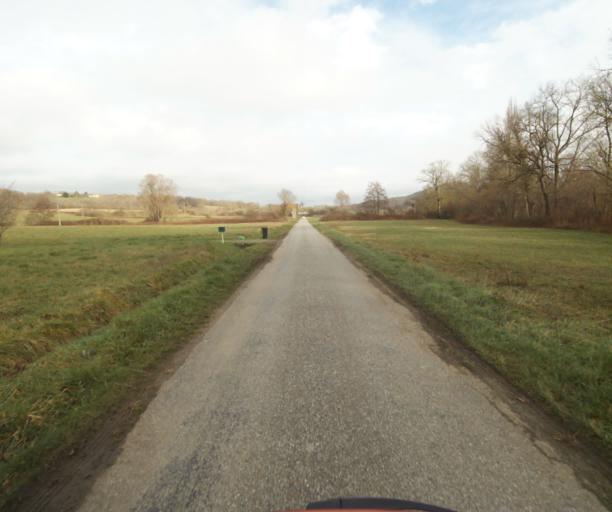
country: FR
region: Midi-Pyrenees
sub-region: Departement de l'Ariege
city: Saverdun
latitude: 43.1826
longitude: 1.5170
